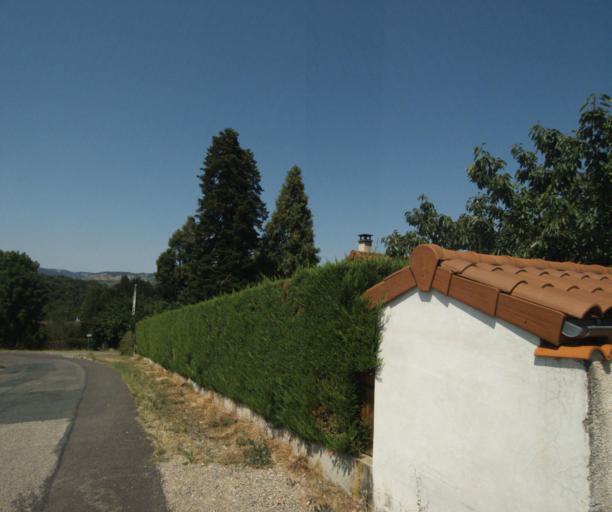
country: FR
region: Rhone-Alpes
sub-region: Departement du Rhone
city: Sourcieux-les-Mines
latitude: 45.8048
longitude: 4.6197
